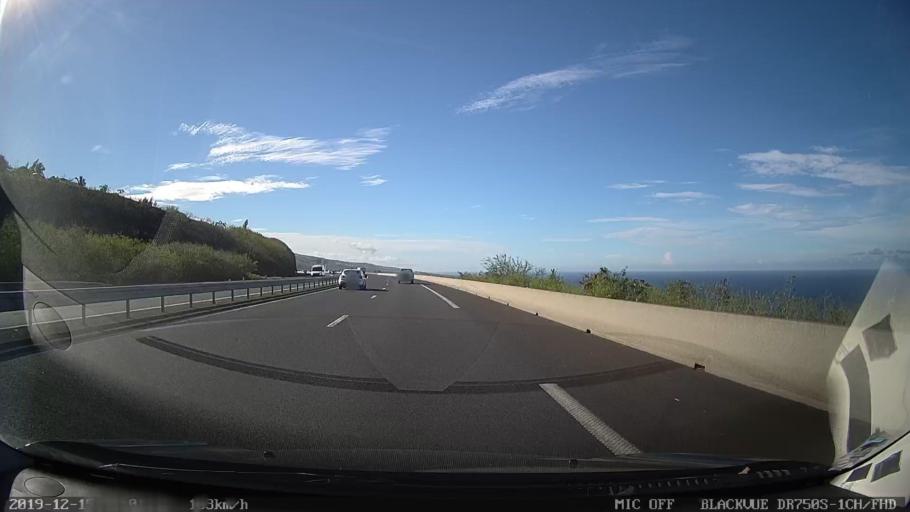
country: RE
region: Reunion
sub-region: Reunion
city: Saint-Leu
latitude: -21.1410
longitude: 55.2855
